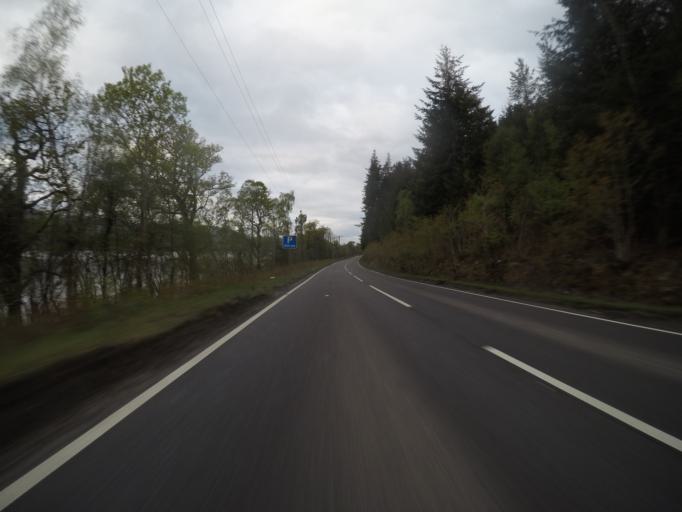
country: GB
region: Scotland
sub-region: Highland
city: Beauly
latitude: 57.1697
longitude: -4.6460
